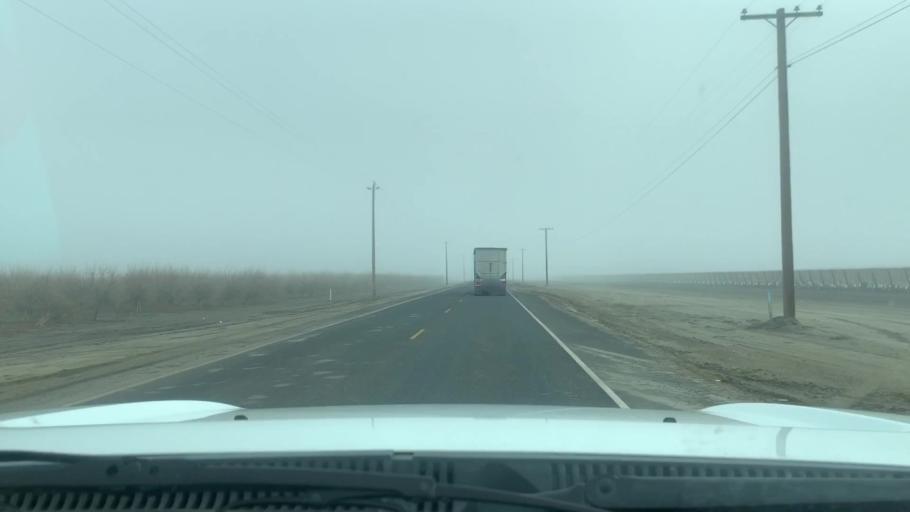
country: US
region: California
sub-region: Kern County
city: Lost Hills
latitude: 35.4995
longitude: -119.6131
